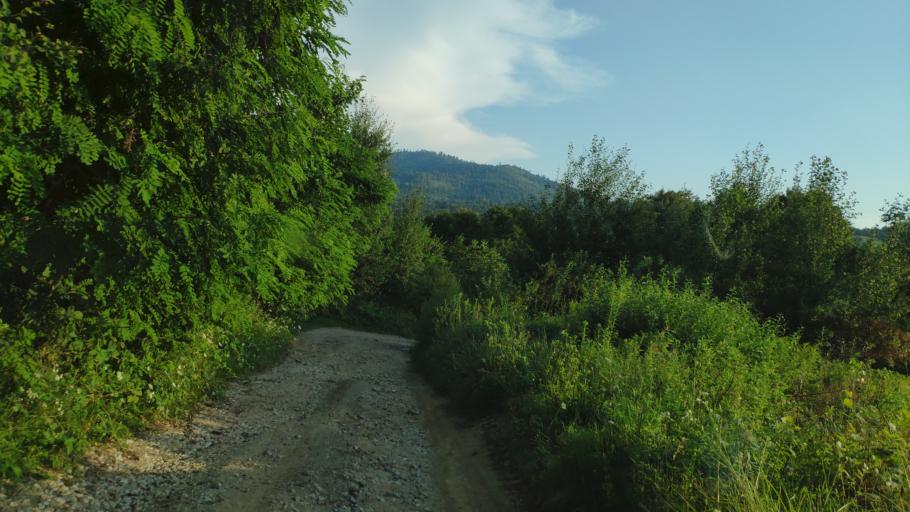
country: SK
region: Kosicky
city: Dobsina
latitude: 48.7157
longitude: 20.2808
